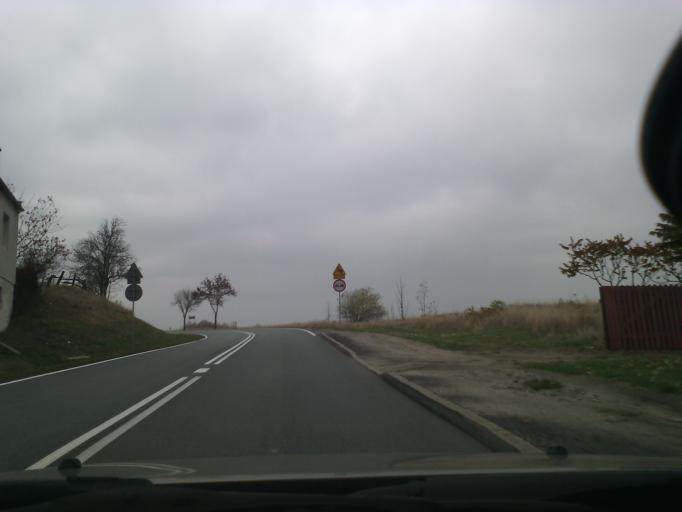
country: PL
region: Lower Silesian Voivodeship
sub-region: Powiat swidnicki
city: Swiebodzice
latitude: 50.8956
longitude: 16.2595
